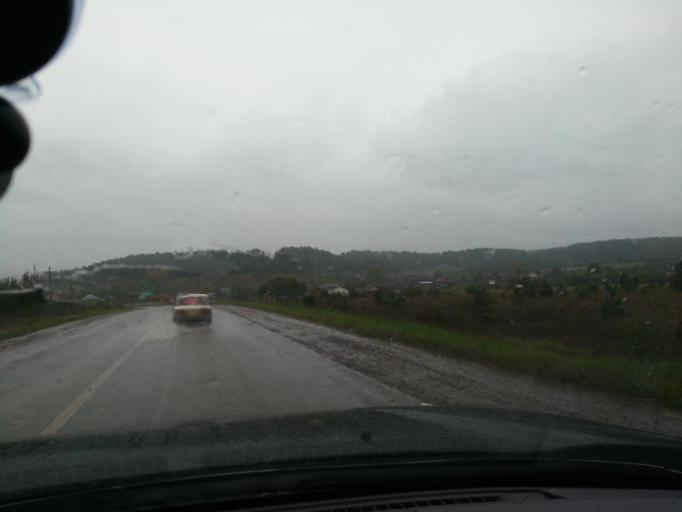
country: RU
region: Perm
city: Osa
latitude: 57.1971
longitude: 55.5919
